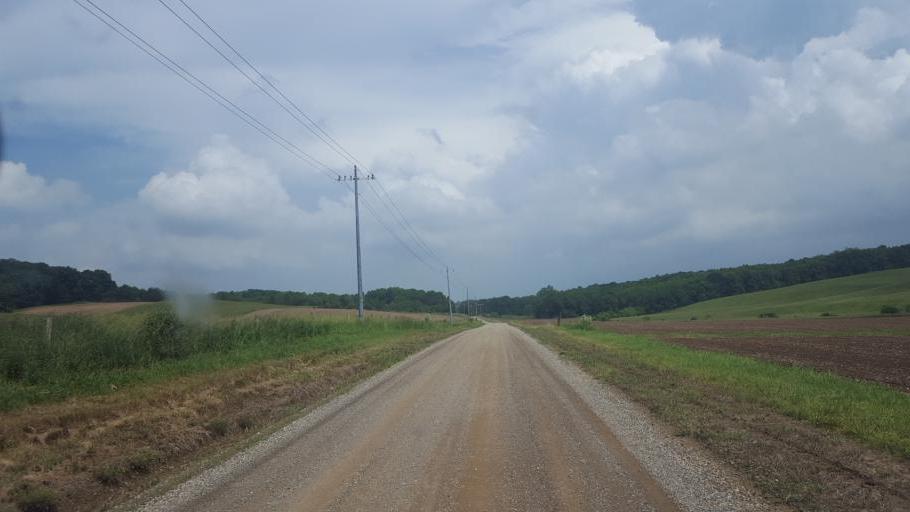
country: US
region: Ohio
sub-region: Knox County
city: Oak Hill
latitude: 40.2740
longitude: -82.2584
